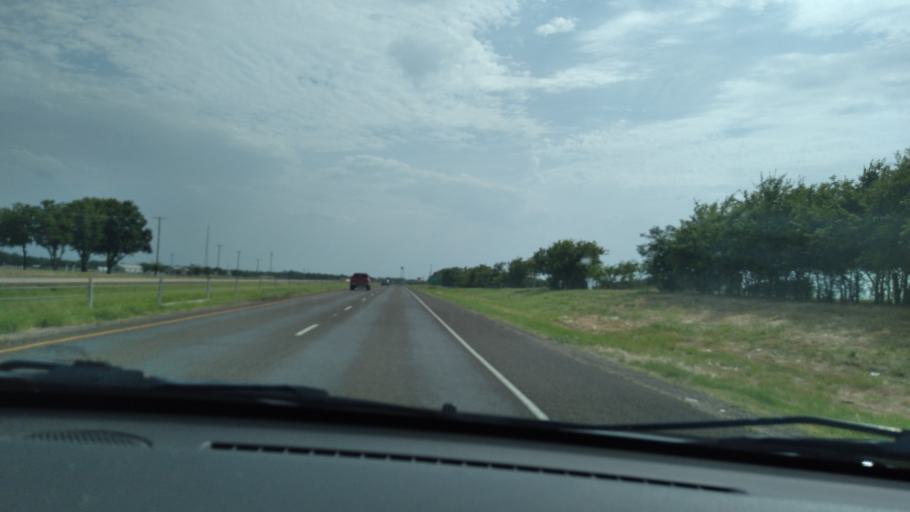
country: US
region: Texas
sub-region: Navarro County
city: Corsicana
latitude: 32.0469
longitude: -96.5366
